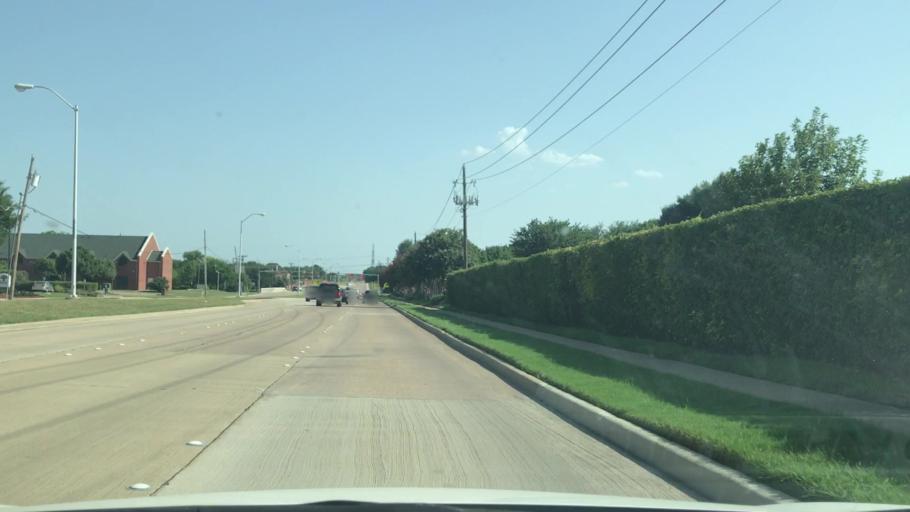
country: US
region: Texas
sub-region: Collin County
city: Plano
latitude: 33.0687
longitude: -96.7505
